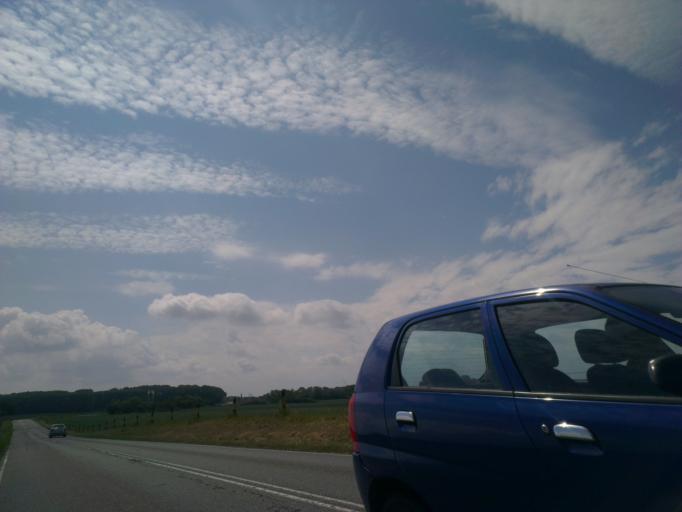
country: DK
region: Capital Region
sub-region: Frederikssund Kommune
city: Jaegerspris
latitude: 55.8675
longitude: 11.9656
